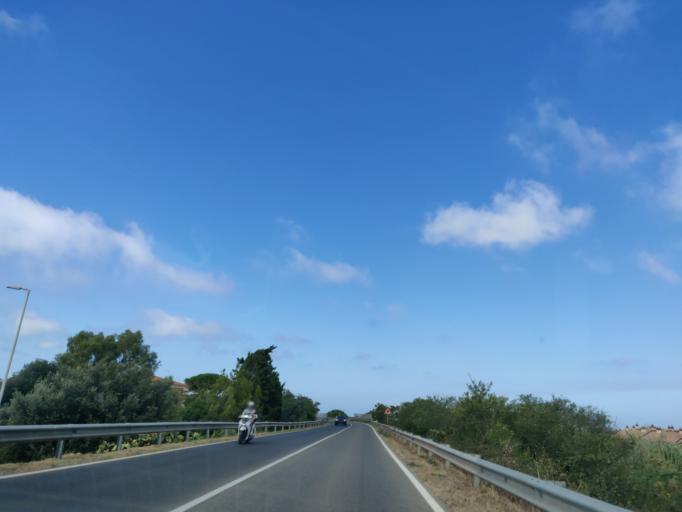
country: IT
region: Tuscany
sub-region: Provincia di Grosseto
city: Orbetello Scalo
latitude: 42.4468
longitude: 11.2461
